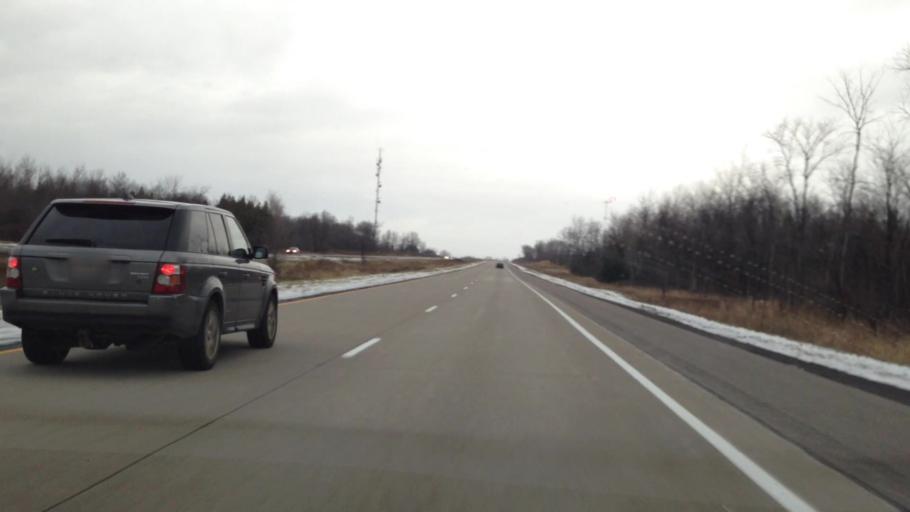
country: CA
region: Ontario
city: Hawkesbury
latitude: 45.5543
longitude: -74.5186
